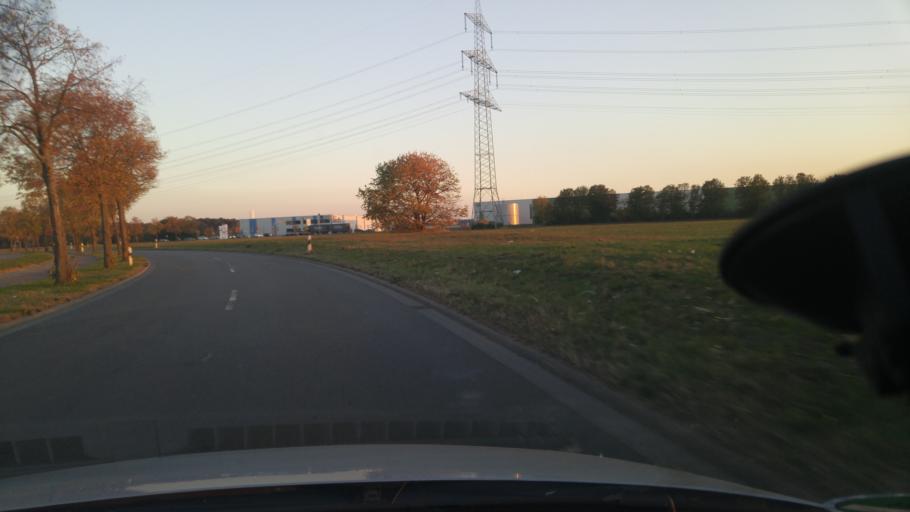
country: DE
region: Hesse
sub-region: Regierungsbezirk Darmstadt
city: Rodgau
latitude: 50.0181
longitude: 8.9001
